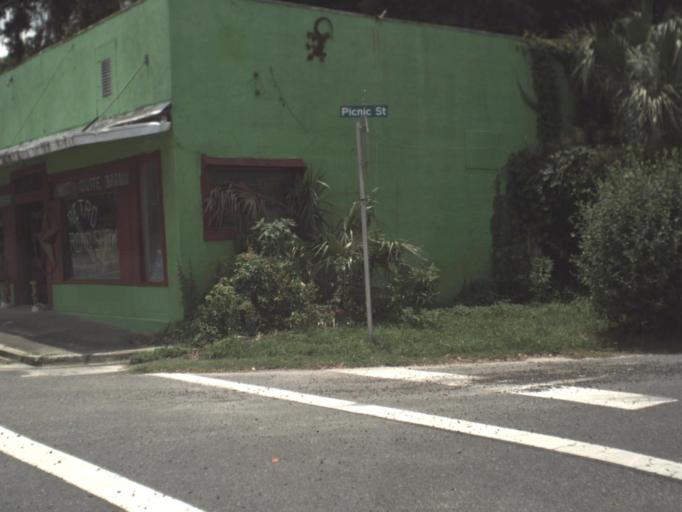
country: US
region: Florida
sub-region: Levy County
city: Bronson
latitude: 29.4452
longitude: -82.6371
